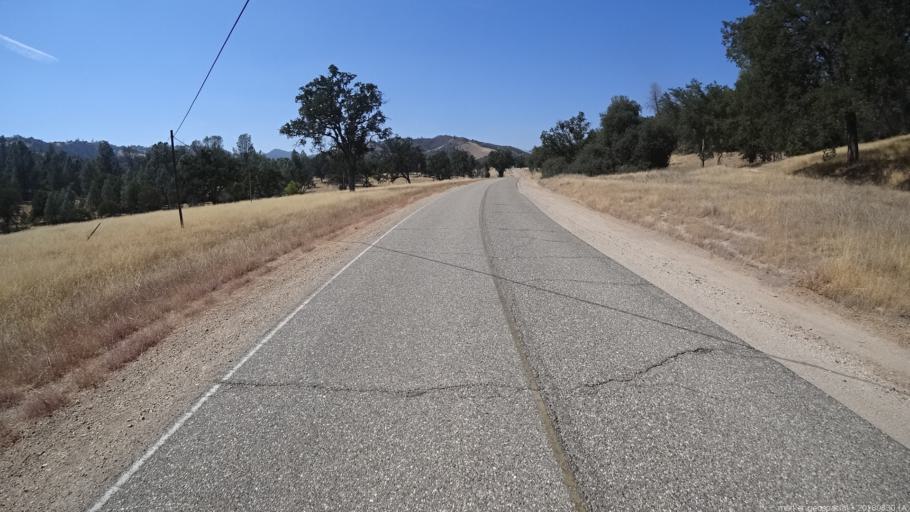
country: US
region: California
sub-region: Monterey County
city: King City
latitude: 36.0067
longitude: -121.2753
